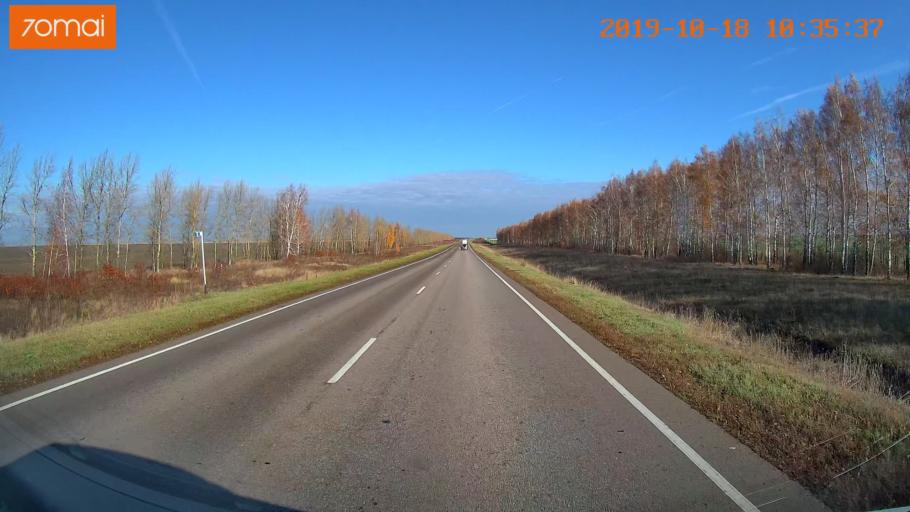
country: RU
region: Tula
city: Kurkino
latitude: 53.5357
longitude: 38.6206
